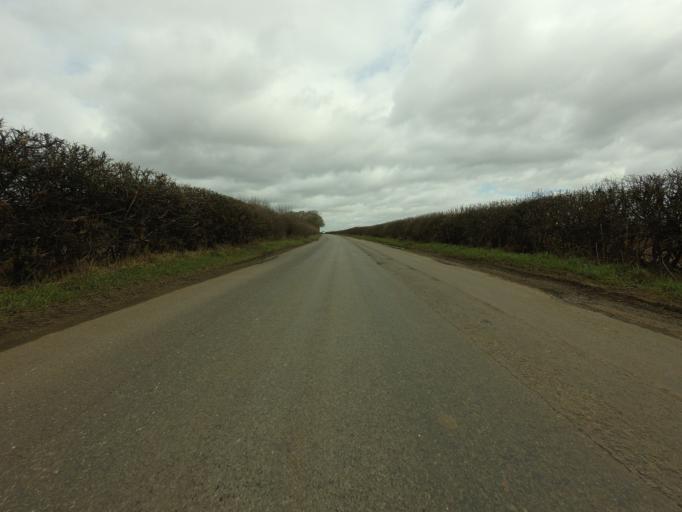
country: GB
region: England
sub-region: Lincolnshire
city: Barrowby
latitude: 52.8754
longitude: -0.6716
